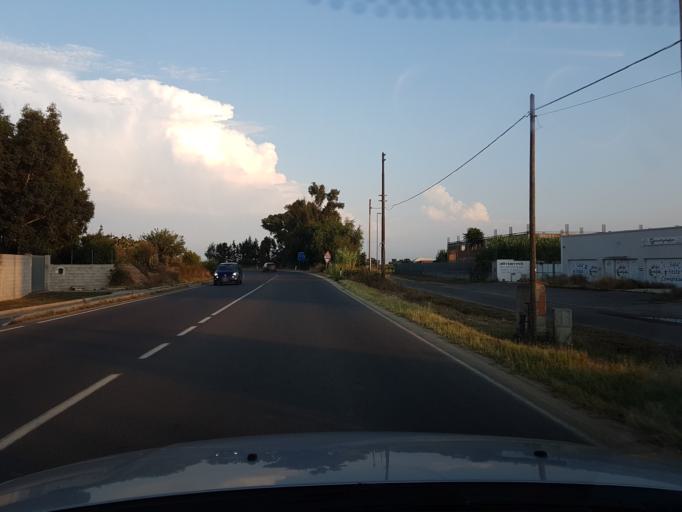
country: IT
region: Sardinia
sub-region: Provincia di Oristano
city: Cabras
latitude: 39.9161
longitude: 8.5405
